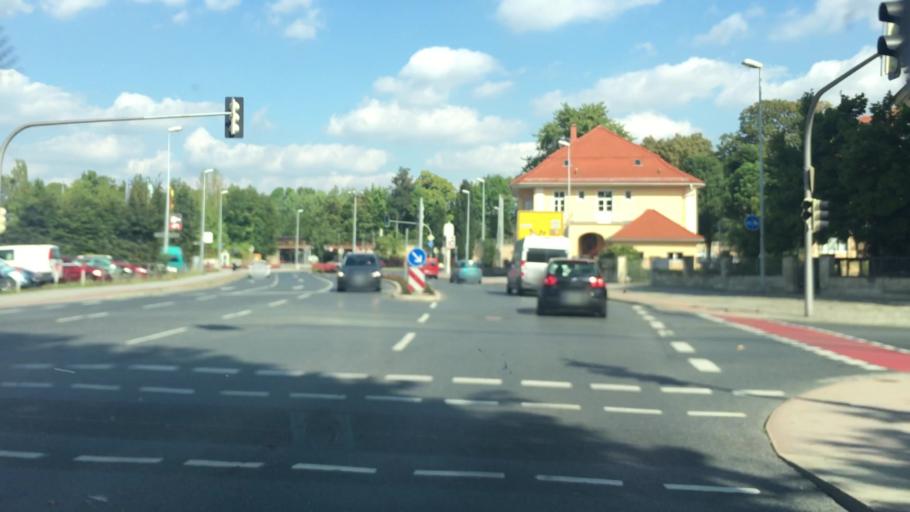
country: DE
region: Saxony
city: Pirna
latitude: 50.9610
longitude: 13.9311
